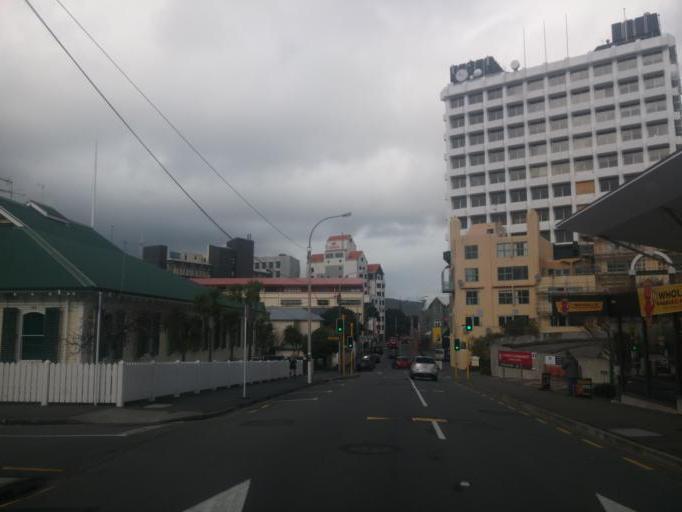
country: NZ
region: Wellington
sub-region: Wellington City
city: Wellington
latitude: -41.2741
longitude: 174.7789
